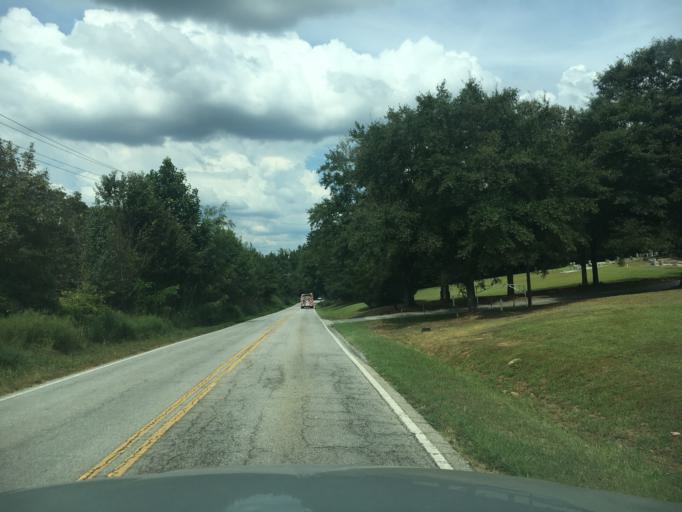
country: US
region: South Carolina
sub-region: Greenville County
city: Five Forks
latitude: 34.8420
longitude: -82.2272
